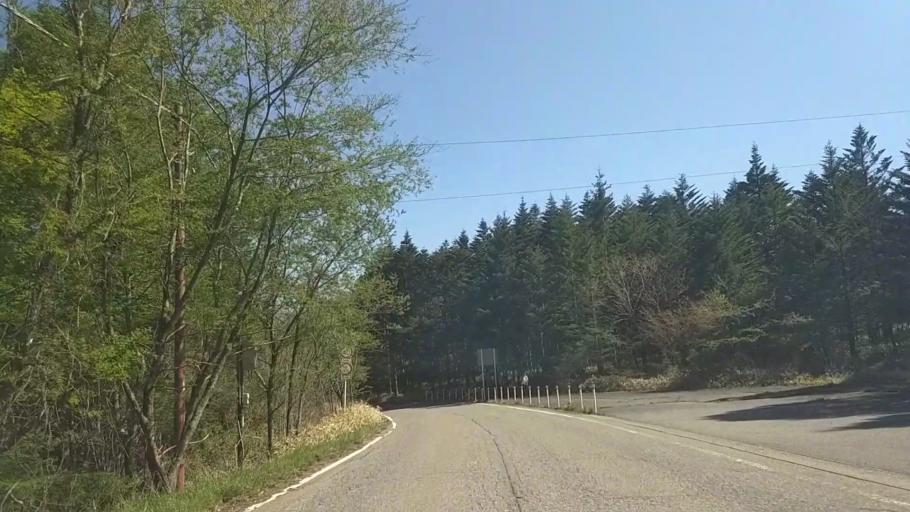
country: JP
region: Yamanashi
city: Nirasaki
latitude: 35.9433
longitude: 138.4198
